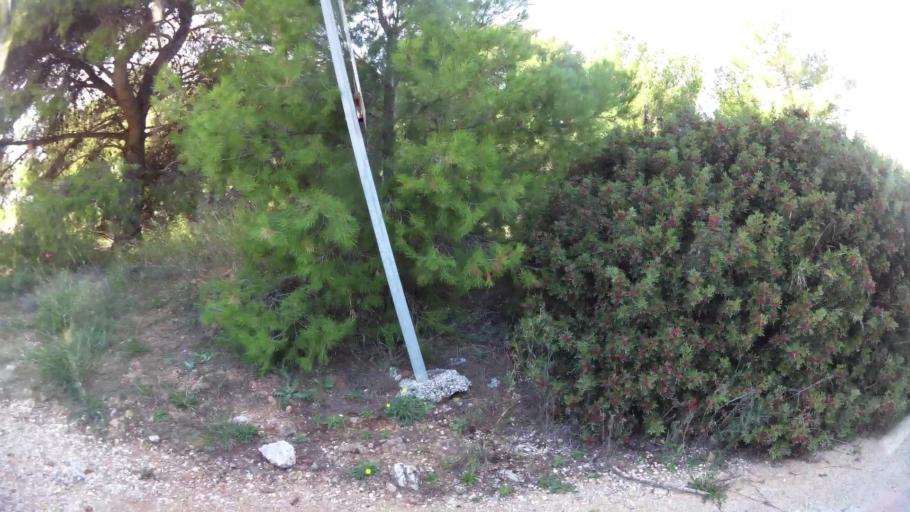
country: GR
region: Attica
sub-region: Nomarchia Anatolikis Attikis
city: Dioni
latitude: 38.0177
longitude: 23.9277
